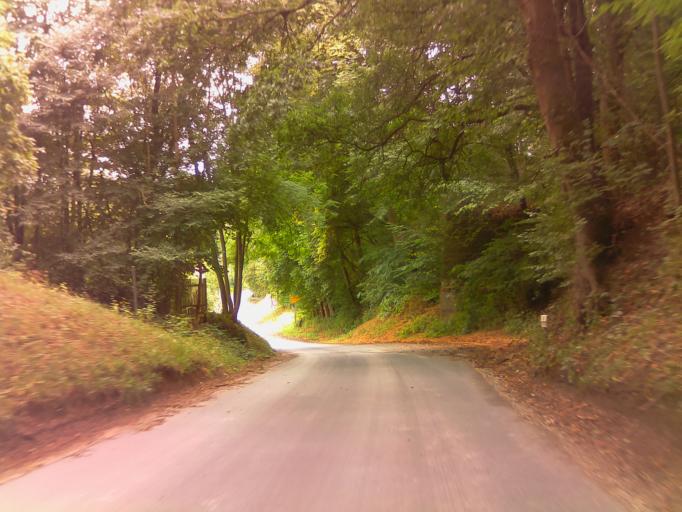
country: DE
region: Thuringia
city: Grosseutersdorf
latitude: 50.7911
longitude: 11.5586
